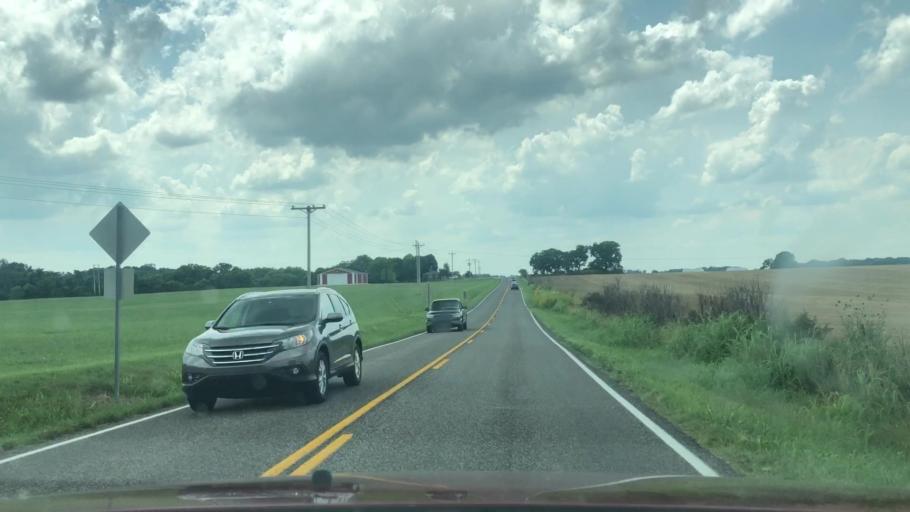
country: US
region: Missouri
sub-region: Christian County
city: Ozark
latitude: 36.9430
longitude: -93.2410
